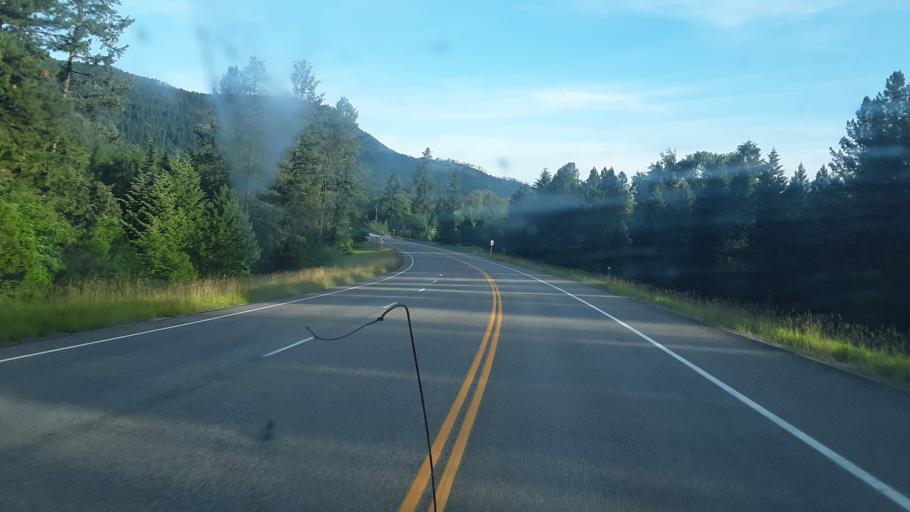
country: US
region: Montana
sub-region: Lincoln County
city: Libby
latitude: 48.4473
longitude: -115.8759
